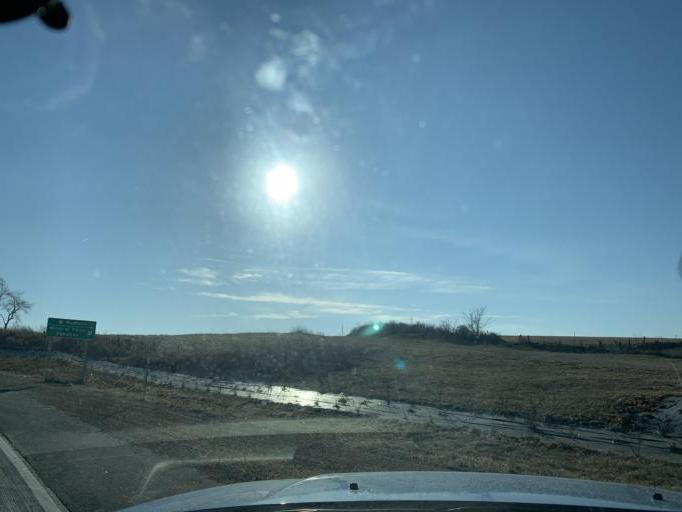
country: US
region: Wisconsin
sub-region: Iowa County
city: Dodgeville
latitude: 42.9398
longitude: -90.1330
